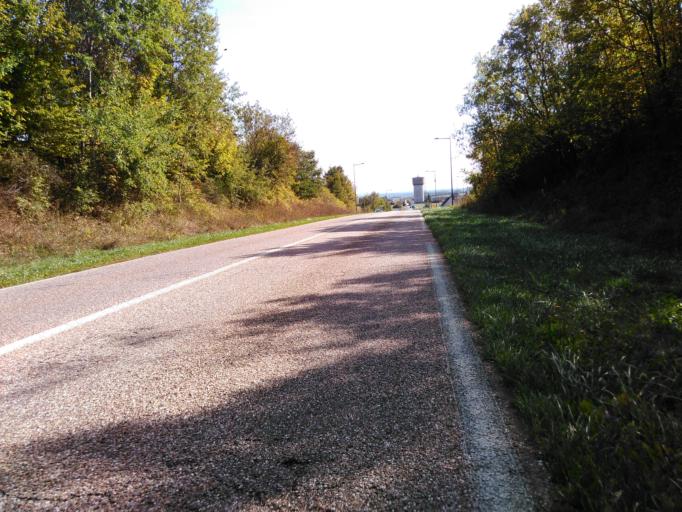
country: FR
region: Lorraine
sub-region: Departement de la Moselle
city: Hettange-Grande
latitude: 49.4190
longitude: 6.1369
